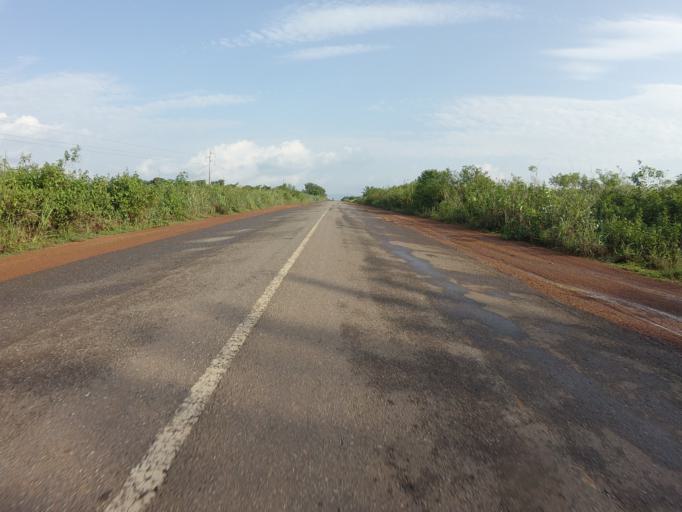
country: GH
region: Volta
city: Hohoe
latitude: 7.0280
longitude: 0.4276
